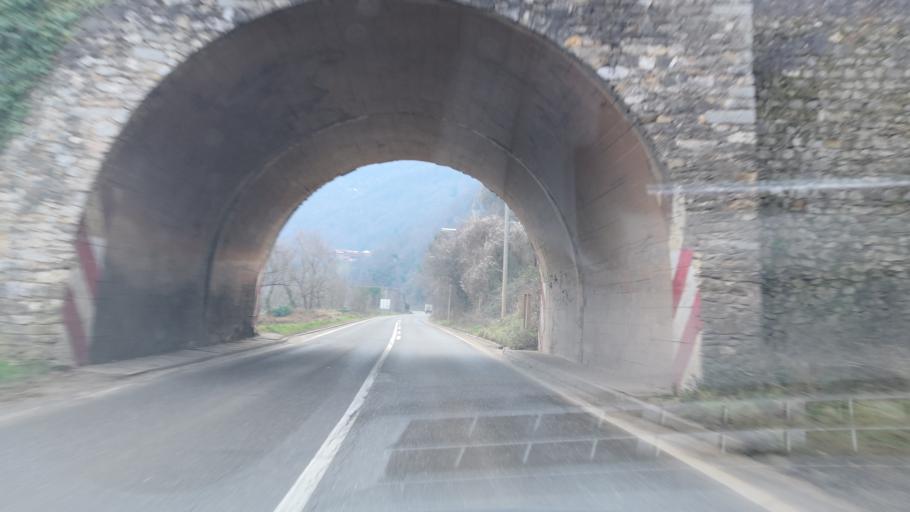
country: RS
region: Central Serbia
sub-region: Macvanski Okrug
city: Mali Zvornik
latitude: 44.3745
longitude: 19.1017
